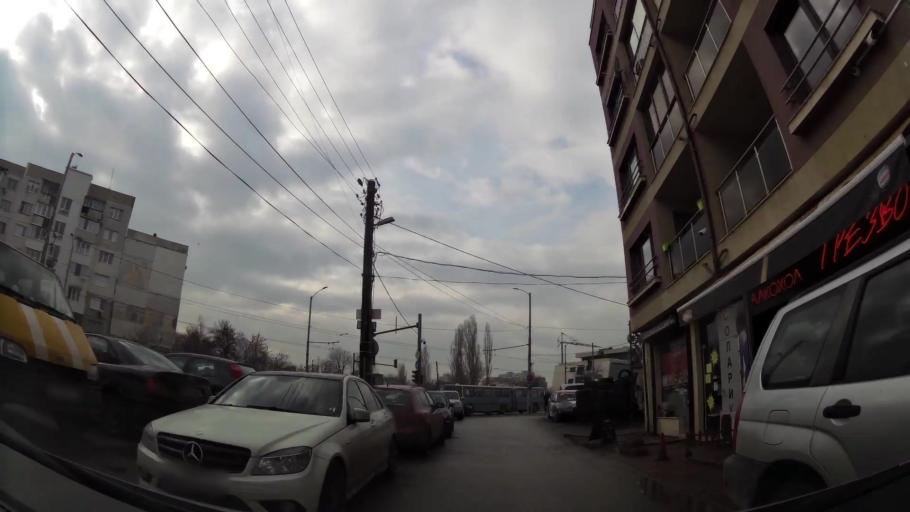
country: BG
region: Sofia-Capital
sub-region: Stolichna Obshtina
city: Sofia
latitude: 42.7149
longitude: 23.2586
